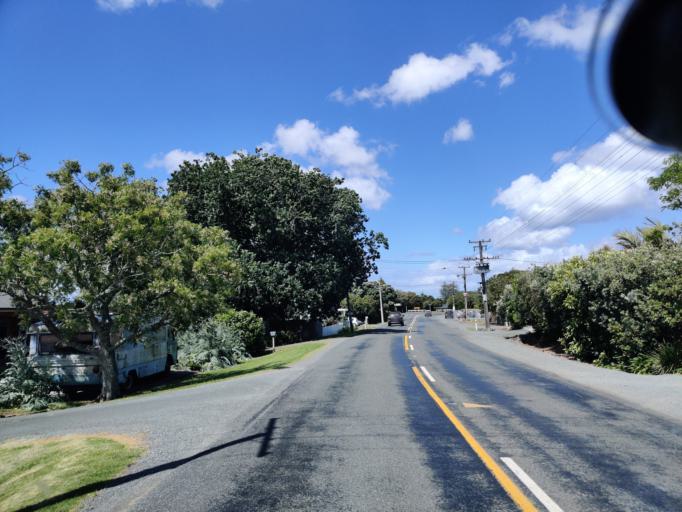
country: NZ
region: Northland
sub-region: Whangarei
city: Ruakaka
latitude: -35.9826
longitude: 174.4378
